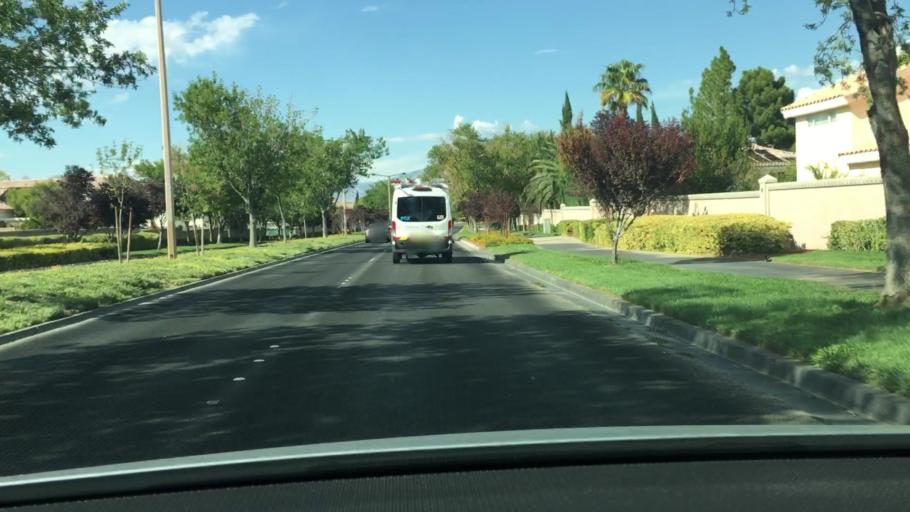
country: US
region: Nevada
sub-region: Clark County
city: Summerlin South
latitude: 36.2005
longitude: -115.3005
